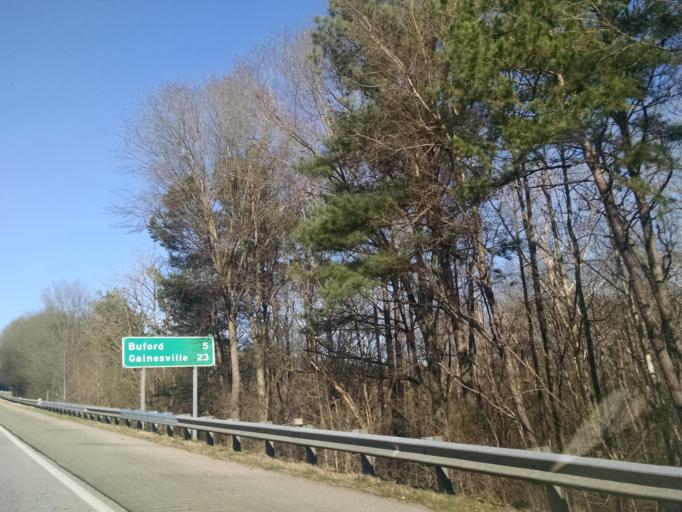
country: US
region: Georgia
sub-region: Gwinnett County
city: Suwanee
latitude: 34.0504
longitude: -84.0272
